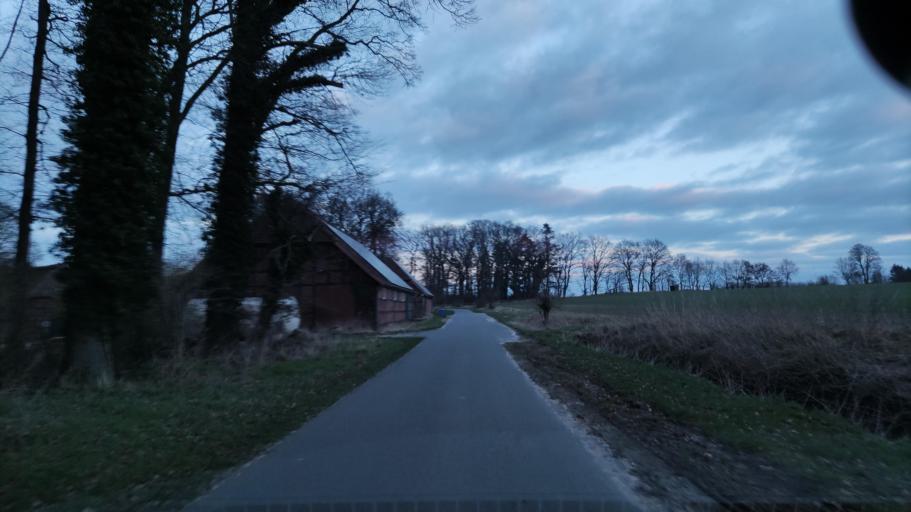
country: DE
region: Lower Saxony
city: Ebstorf
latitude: 53.0721
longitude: 10.4257
